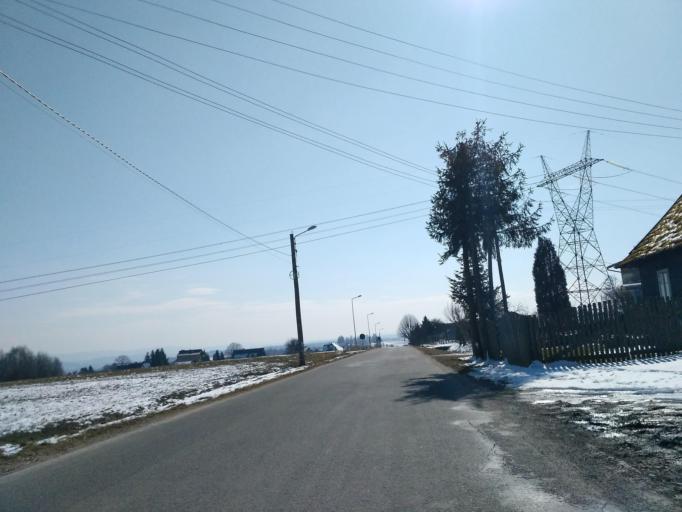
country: PL
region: Subcarpathian Voivodeship
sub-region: Powiat brzozowski
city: Jasienica Rosielna
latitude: 49.7682
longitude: 21.9222
